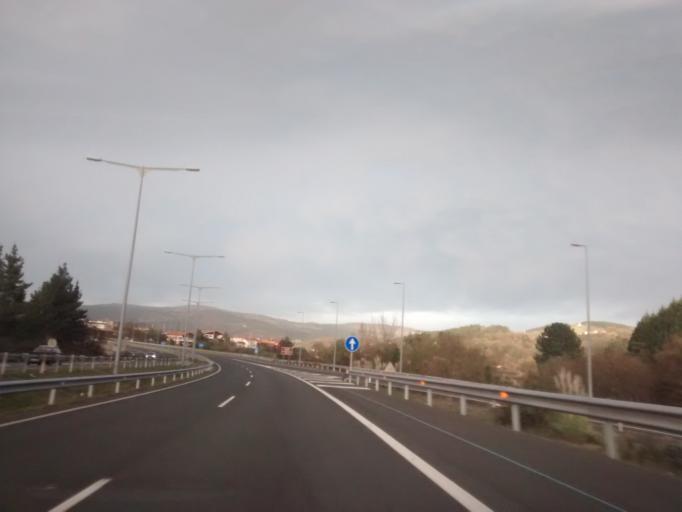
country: ES
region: Basque Country
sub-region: Bizkaia
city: Arrigorriaga
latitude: 43.2008
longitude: -2.8937
